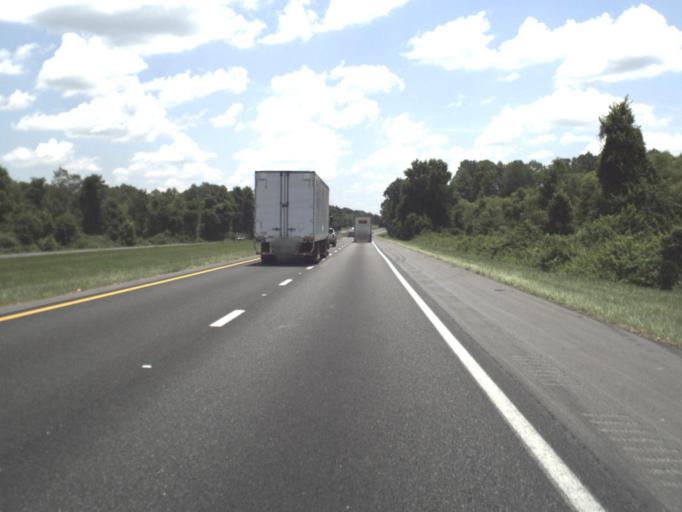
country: US
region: Florida
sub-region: Madison County
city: Madison
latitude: 30.4352
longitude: -83.4809
